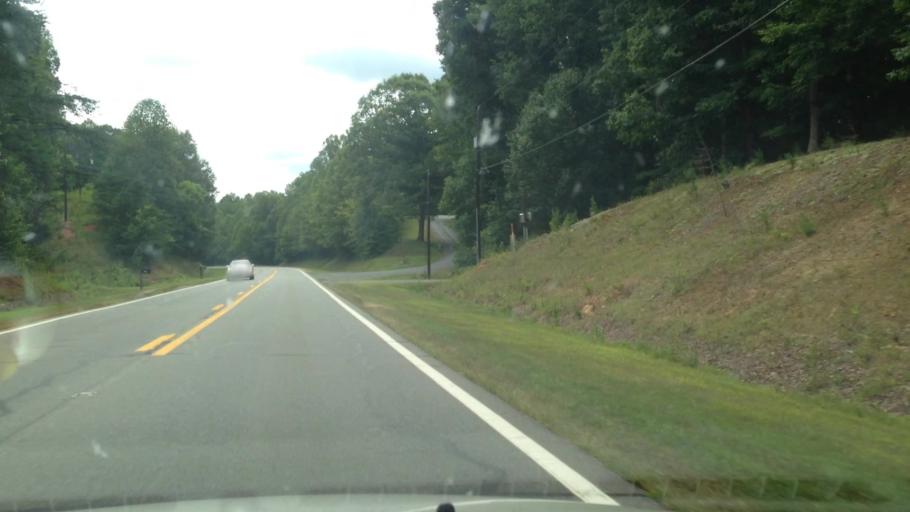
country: US
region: North Carolina
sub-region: Rockingham County
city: Madison
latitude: 36.3793
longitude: -79.8854
